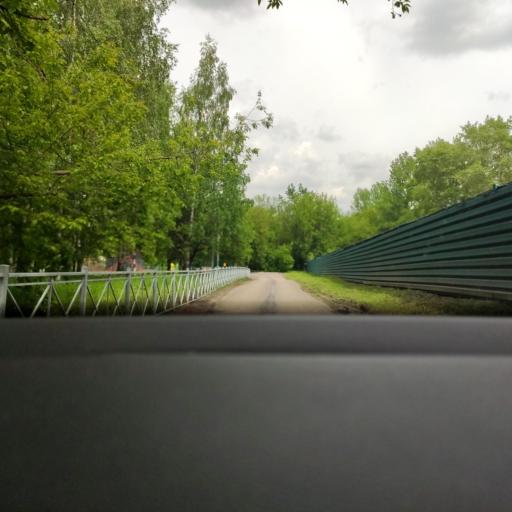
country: RU
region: Moscow
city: Vatutino
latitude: 55.8784
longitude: 37.6628
